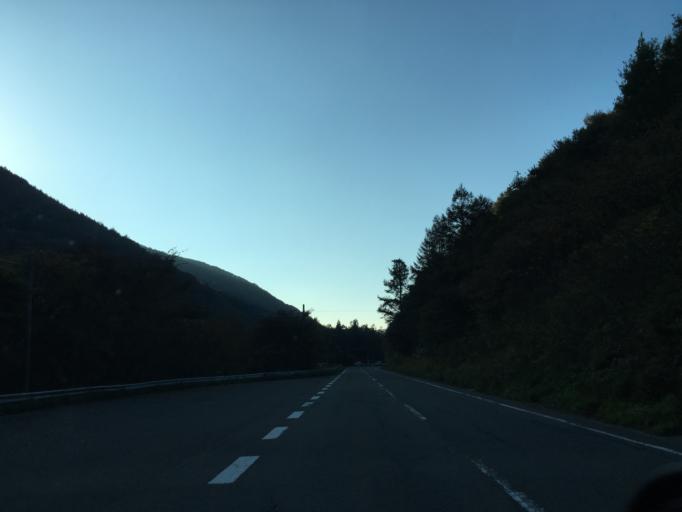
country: JP
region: Fukushima
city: Inawashiro
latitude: 37.3951
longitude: 140.1688
